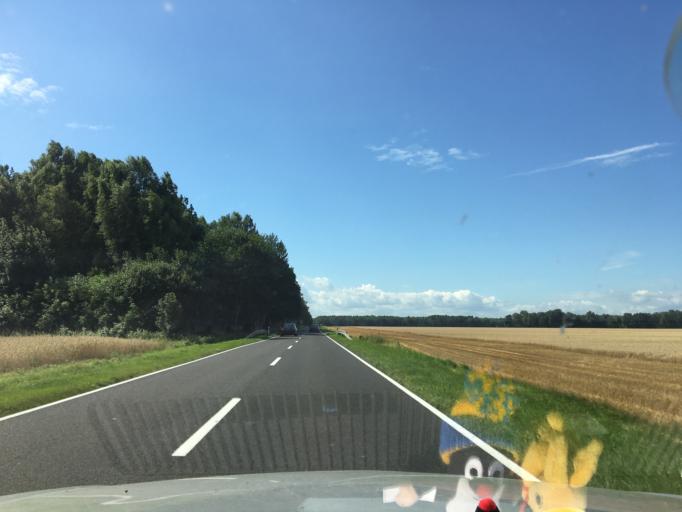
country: PL
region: West Pomeranian Voivodeship
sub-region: Powiat kamienski
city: Kamien Pomorski
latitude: 53.8801
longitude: 14.7838
